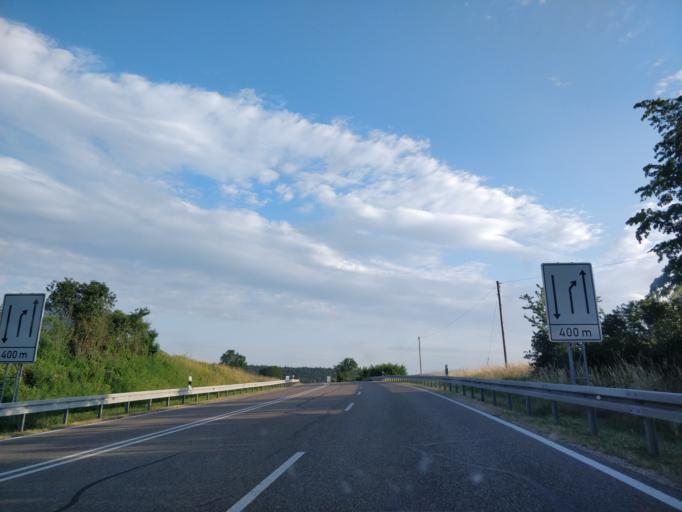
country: DE
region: Bavaria
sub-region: Swabia
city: Ederheim
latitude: 48.8182
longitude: 10.4571
